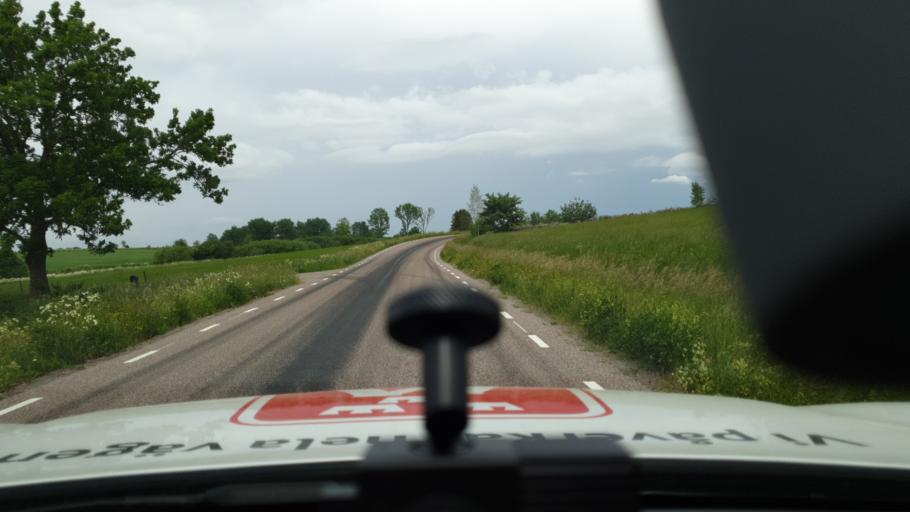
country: SE
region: Vaestra Goetaland
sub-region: Falkopings Kommun
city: Akarp
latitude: 58.1858
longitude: 13.7016
